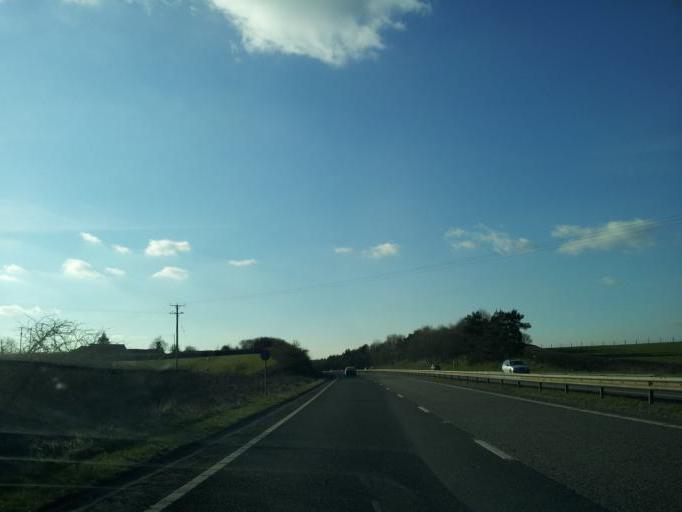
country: GB
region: England
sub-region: Devon
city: Crediton
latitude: 50.7283
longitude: -3.6695
